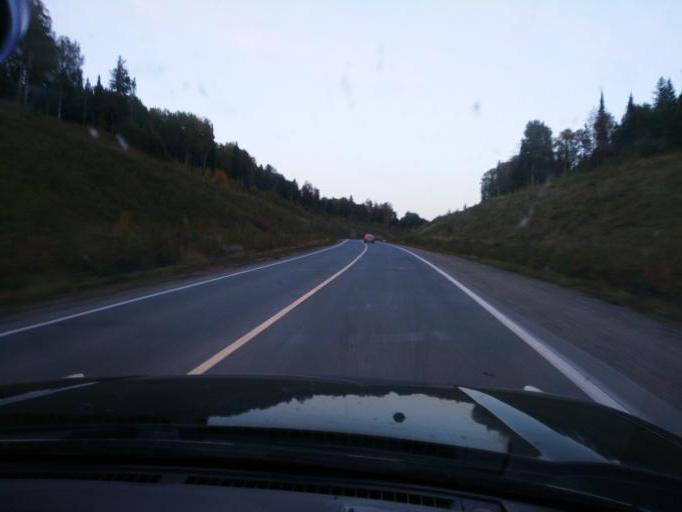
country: RU
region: Perm
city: Sylva
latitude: 58.2955
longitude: 56.8075
